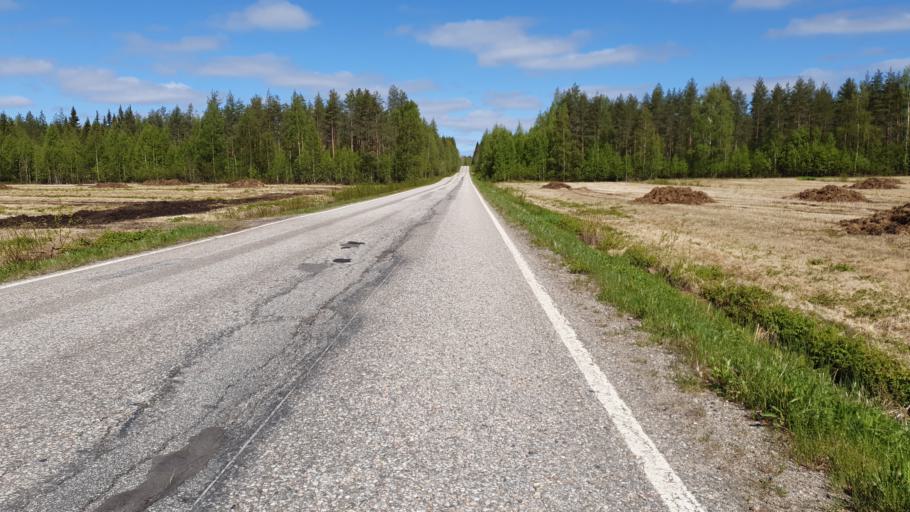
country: FI
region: Kainuu
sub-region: Kehys-Kainuu
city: Kuhmo
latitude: 64.2007
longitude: 29.4516
